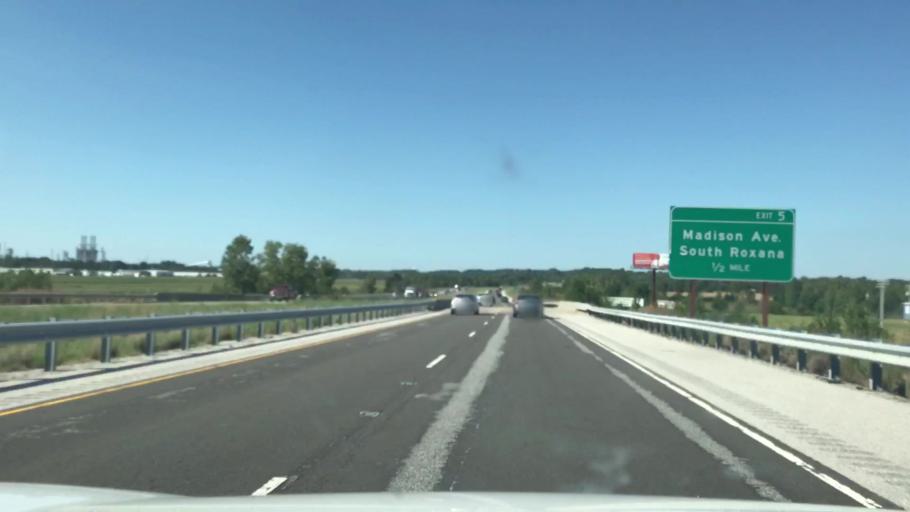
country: US
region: Illinois
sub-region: Madison County
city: South Roxana
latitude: 38.8195
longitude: -90.0421
